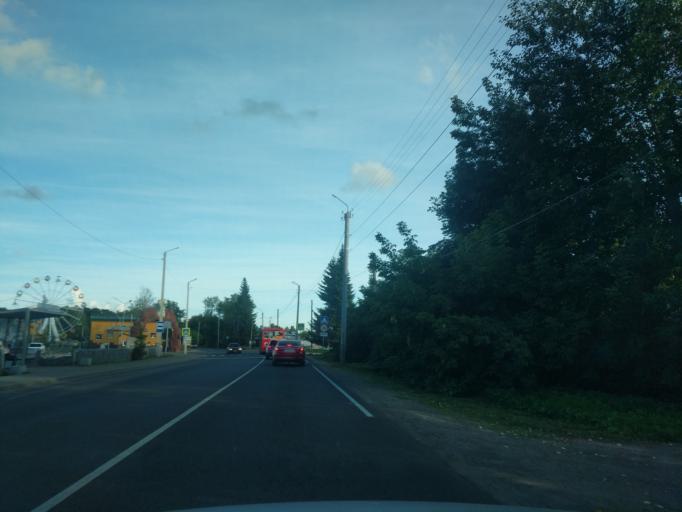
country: RU
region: Kirov
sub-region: Kirovo-Chepetskiy Rayon
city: Kirov
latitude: 58.6131
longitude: 49.7795
